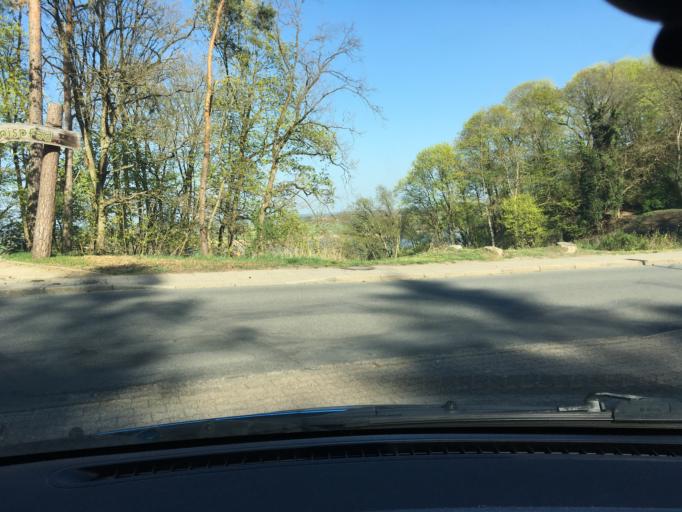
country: DE
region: Lower Saxony
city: Hitzacker
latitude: 53.1549
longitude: 11.0410
